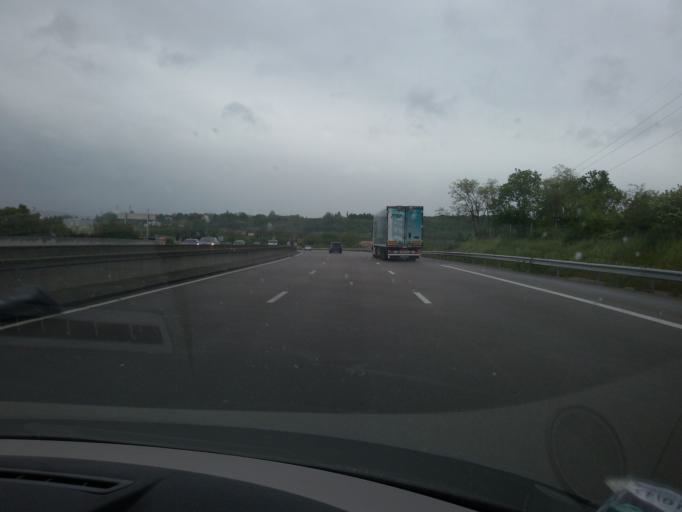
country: FR
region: Rhone-Alpes
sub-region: Departement de l'Isere
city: Chanas
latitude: 45.2951
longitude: 4.8239
